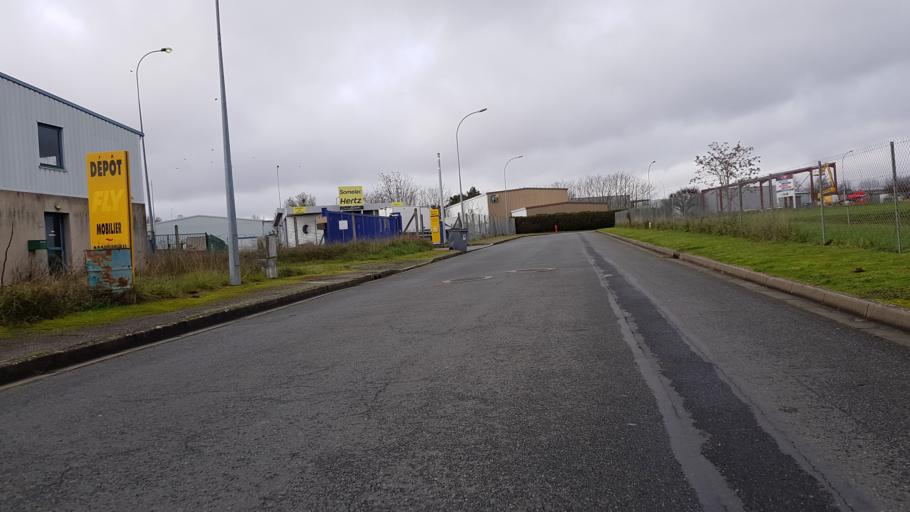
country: FR
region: Poitou-Charentes
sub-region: Departement de la Vienne
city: Chasseneuil-du-Poitou
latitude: 46.6559
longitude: 0.3723
